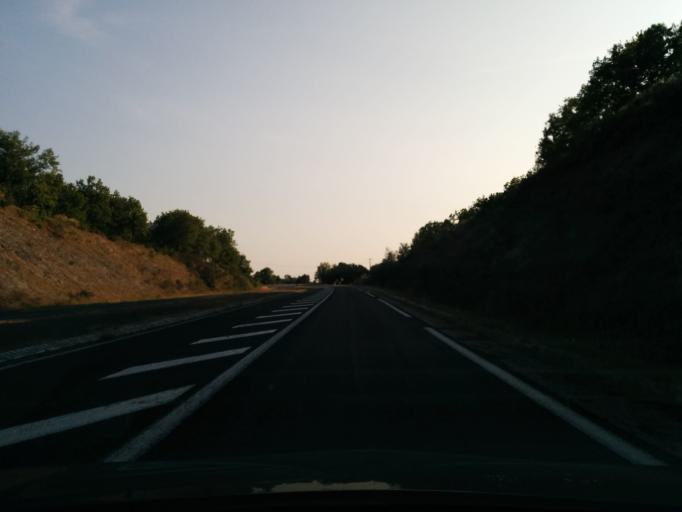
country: FR
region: Midi-Pyrenees
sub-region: Departement du Lot
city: Le Vigan
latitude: 44.8043
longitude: 1.4771
